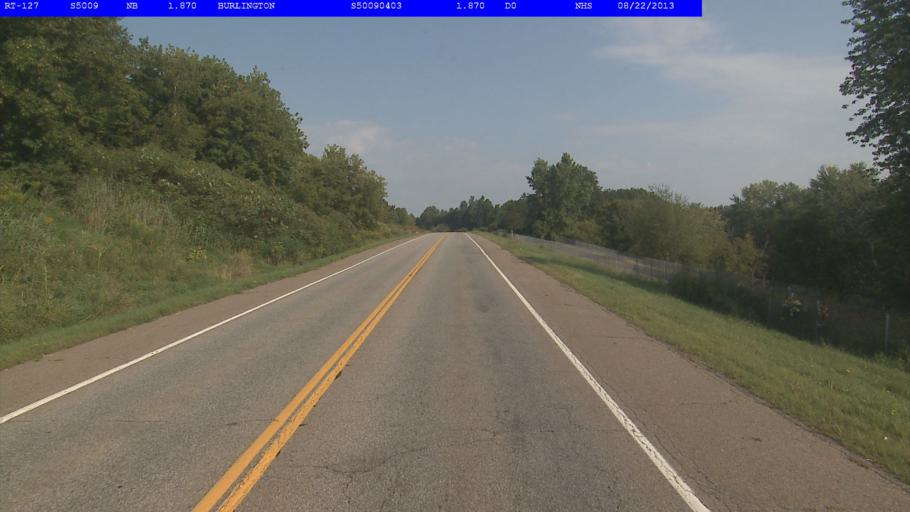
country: US
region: Vermont
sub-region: Chittenden County
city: Burlington
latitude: 44.5113
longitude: -73.2338
